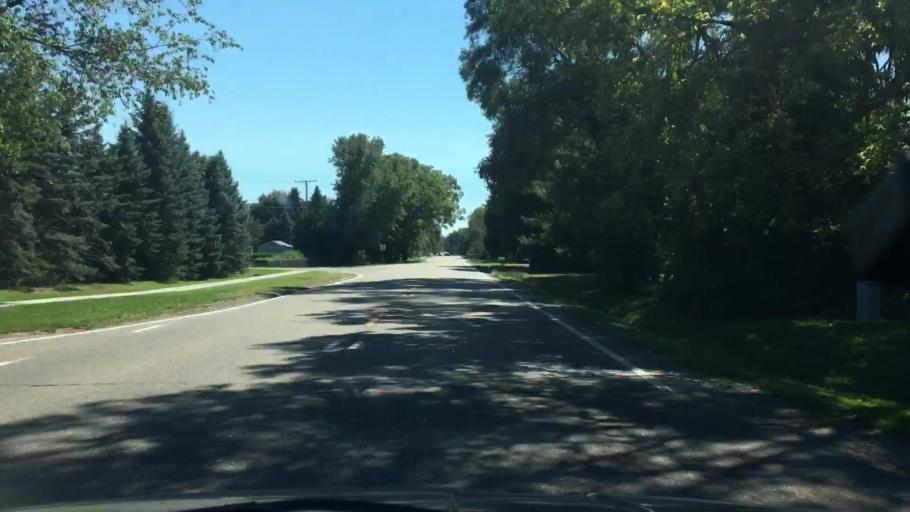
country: US
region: Michigan
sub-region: Livingston County
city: Brighton
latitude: 42.5115
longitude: -83.7692
